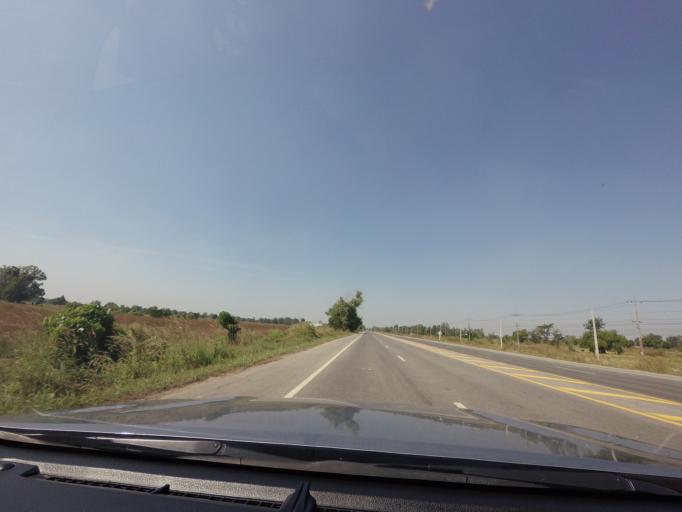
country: TH
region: Sukhothai
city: Ban Na
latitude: 17.0423
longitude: 99.7262
